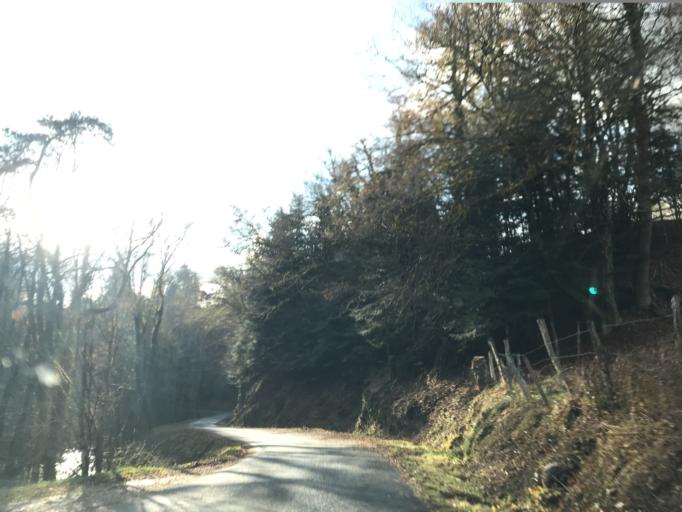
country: FR
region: Auvergne
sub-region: Departement du Puy-de-Dome
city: Escoutoux
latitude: 45.7649
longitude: 3.6319
